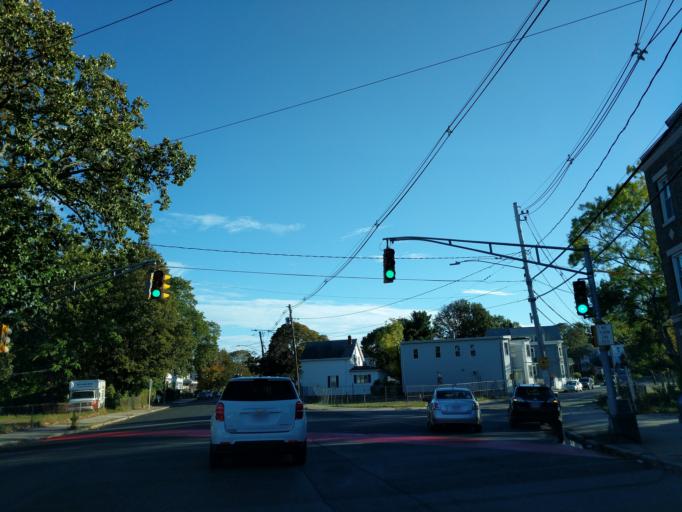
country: US
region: Massachusetts
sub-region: Suffolk County
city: Chelsea
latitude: 42.4096
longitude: -71.0301
